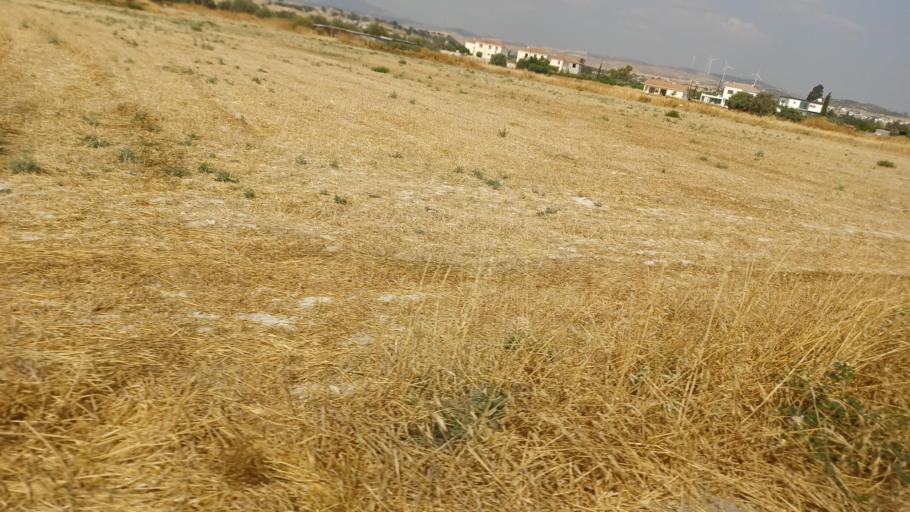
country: CY
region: Larnaka
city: Aradippou
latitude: 34.9245
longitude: 33.5404
